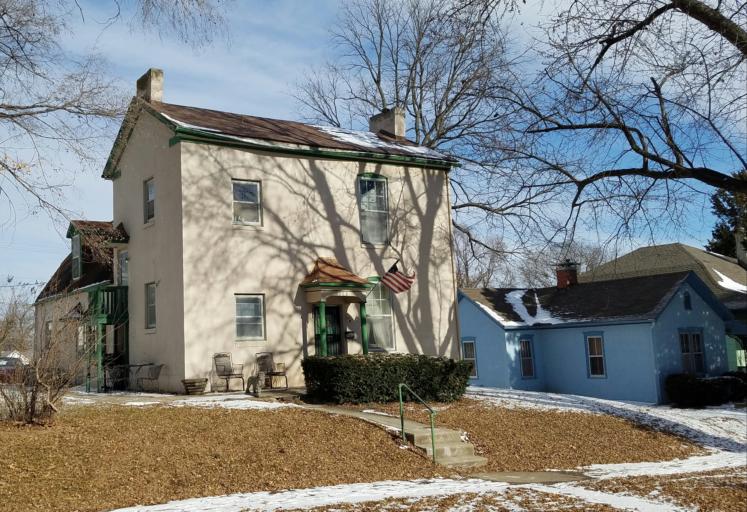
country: US
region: Missouri
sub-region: Lafayette County
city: Lexington
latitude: 39.1833
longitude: -93.8714
